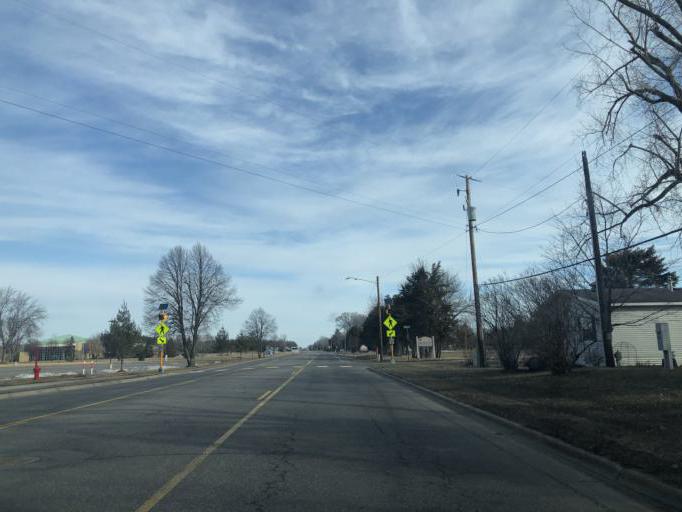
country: US
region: Minnesota
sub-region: Sherburne County
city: Becker
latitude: 45.3983
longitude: -93.8703
